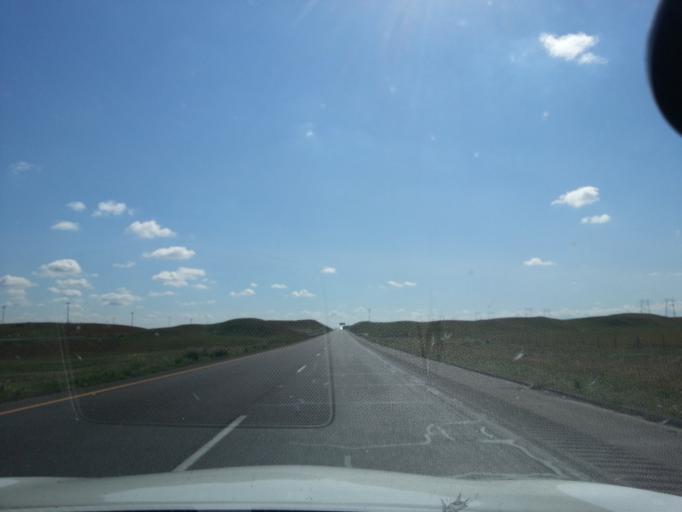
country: US
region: California
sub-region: Fresno County
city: Coalinga
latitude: 36.3154
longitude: -120.2875
